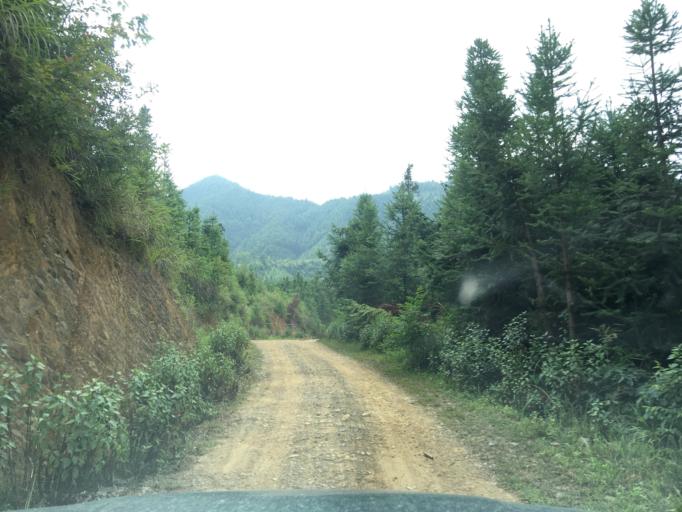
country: CN
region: Guangxi Zhuangzu Zizhiqu
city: Xinzhou
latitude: 24.8854
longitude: 105.8423
